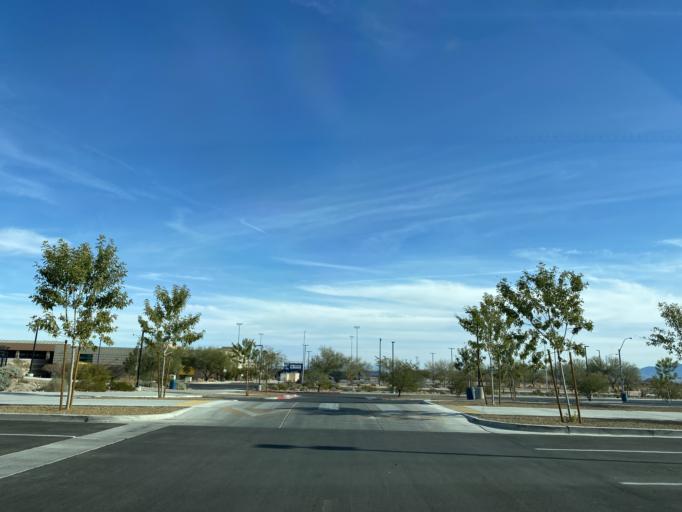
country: US
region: Nevada
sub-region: Clark County
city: Enterprise
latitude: 36.0490
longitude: -115.2713
